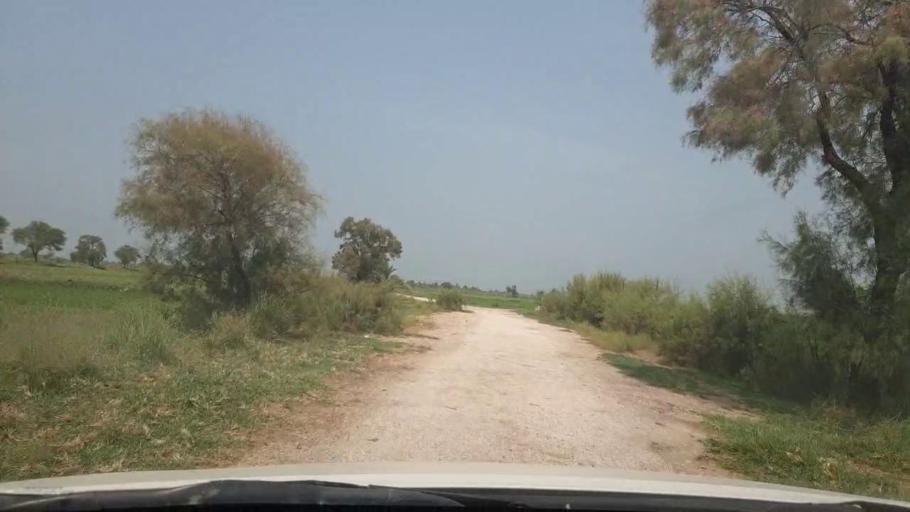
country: PK
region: Sindh
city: Rustam jo Goth
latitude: 28.0483
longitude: 68.7511
